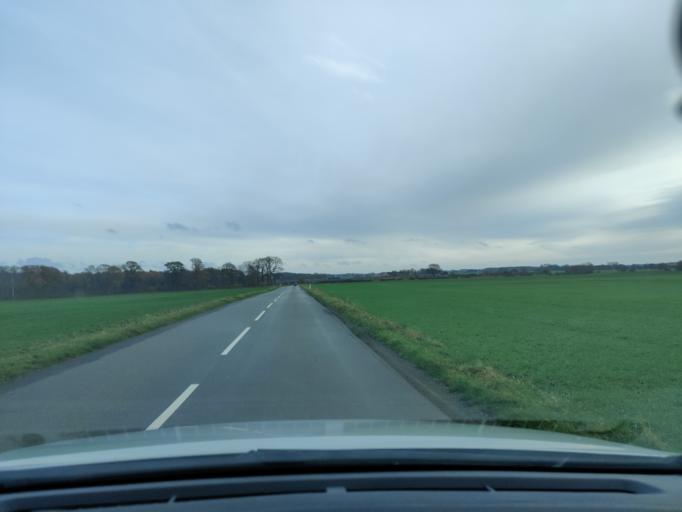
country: DK
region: South Denmark
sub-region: Kerteminde Kommune
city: Munkebo
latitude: 55.4256
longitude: 10.5404
